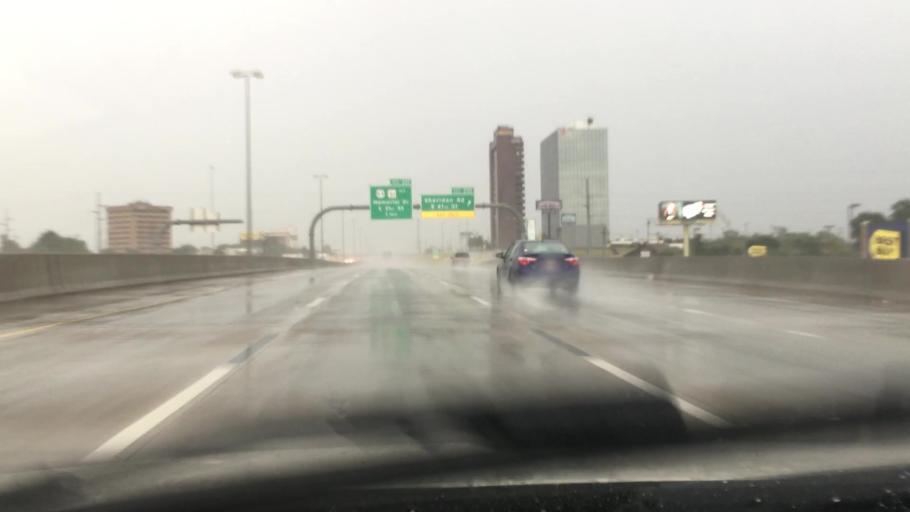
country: US
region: Oklahoma
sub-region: Tulsa County
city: Jenks
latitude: 36.0999
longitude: -95.9157
